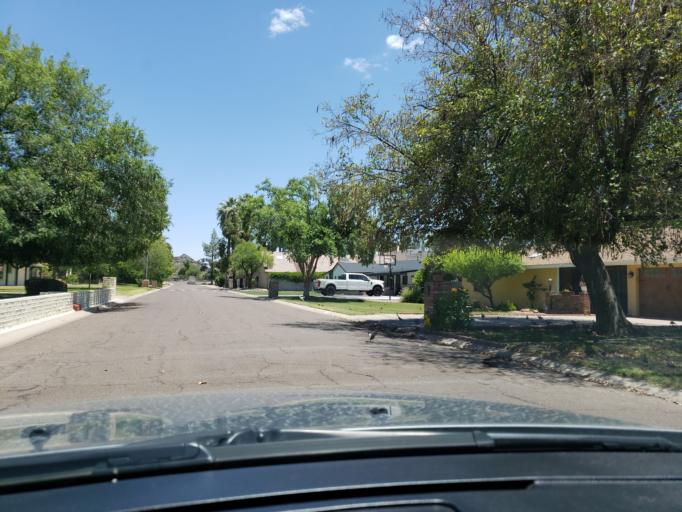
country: US
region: Arizona
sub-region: Maricopa County
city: Glendale
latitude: 33.5620
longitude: -112.0759
